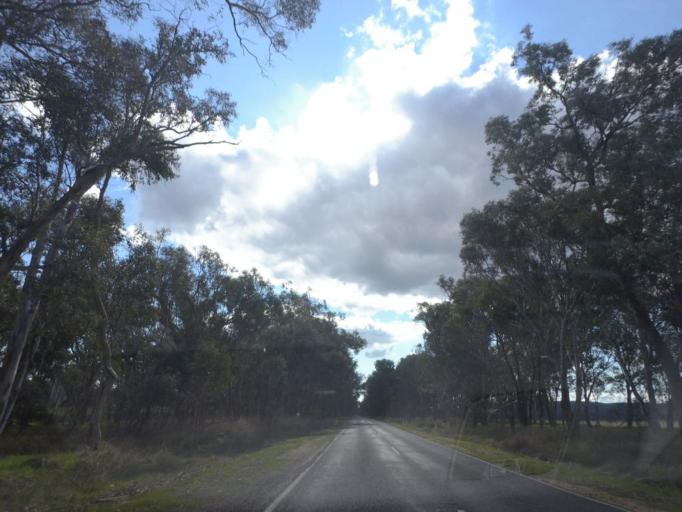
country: AU
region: New South Wales
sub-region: Corowa Shire
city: Howlong
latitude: -36.2066
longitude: 146.6219
